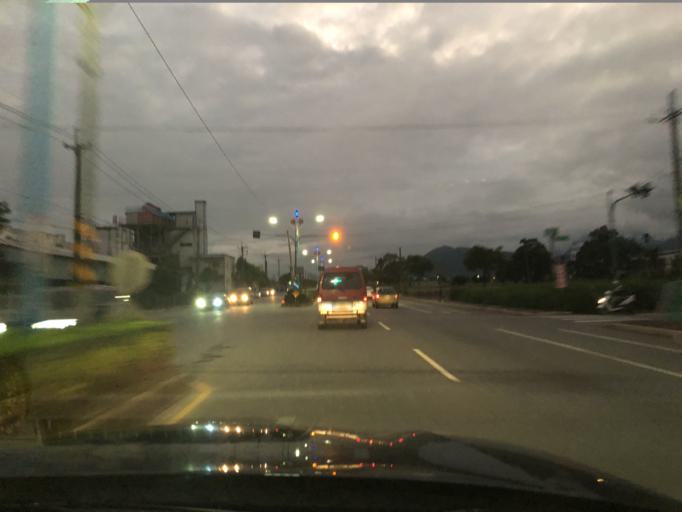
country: TW
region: Taiwan
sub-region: Hualien
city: Hualian
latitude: 23.9693
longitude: 121.5700
